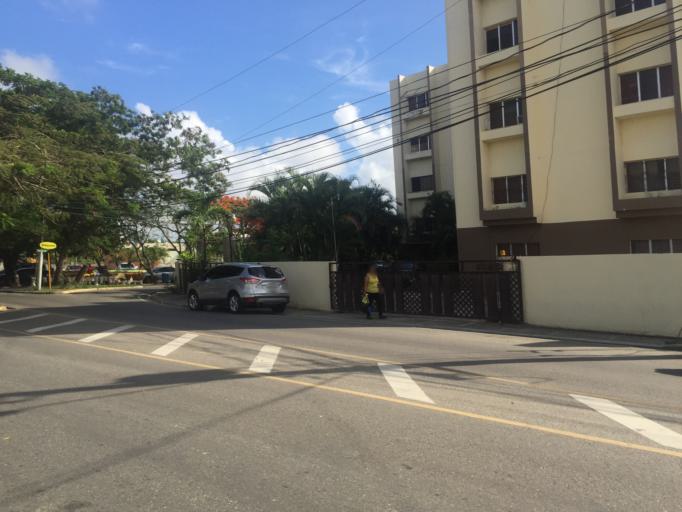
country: DO
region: Santiago
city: Santiago de los Caballeros
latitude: 19.4450
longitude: -70.6704
